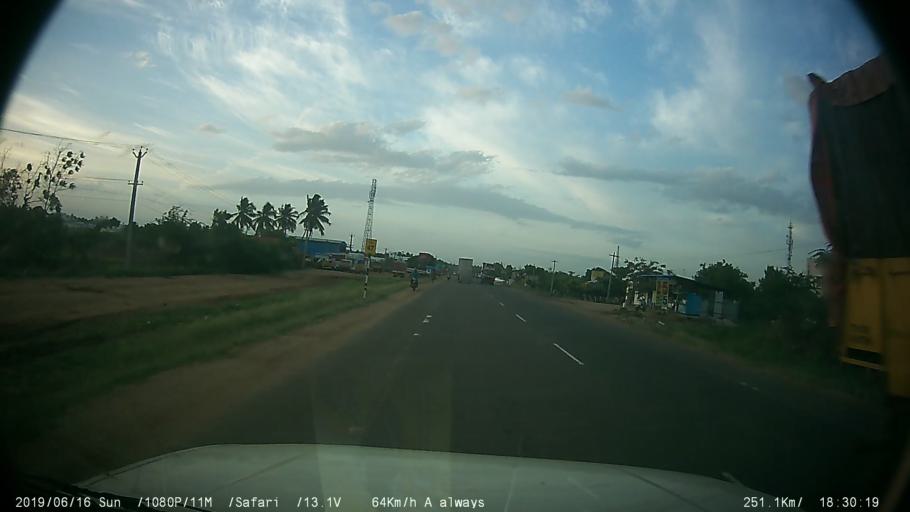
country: IN
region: Tamil Nadu
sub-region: Coimbatore
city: Irugur
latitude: 11.0295
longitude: 77.0763
